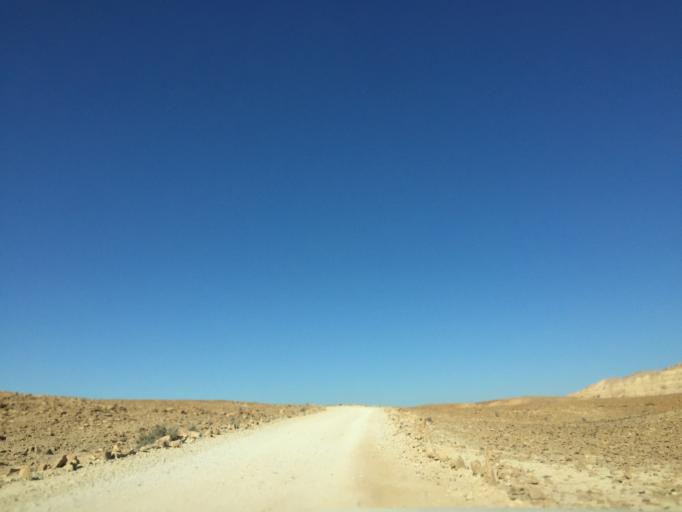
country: IL
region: Southern District
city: Mitzpe Ramon
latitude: 30.6181
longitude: 34.9305
